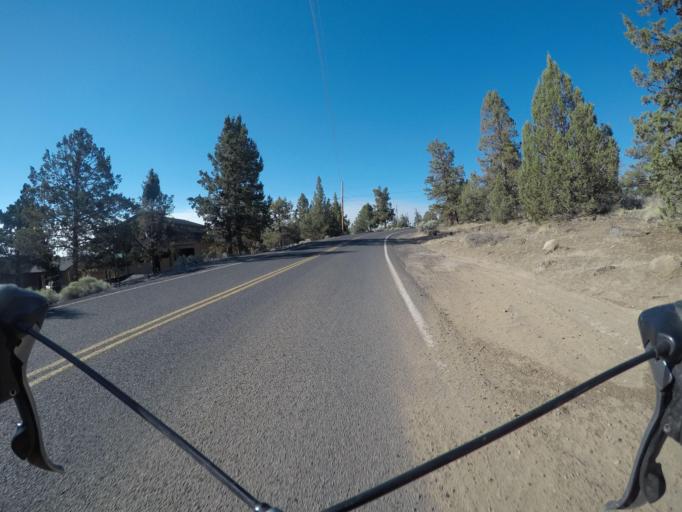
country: US
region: Oregon
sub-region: Deschutes County
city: Bend
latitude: 44.1782
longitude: -121.2660
